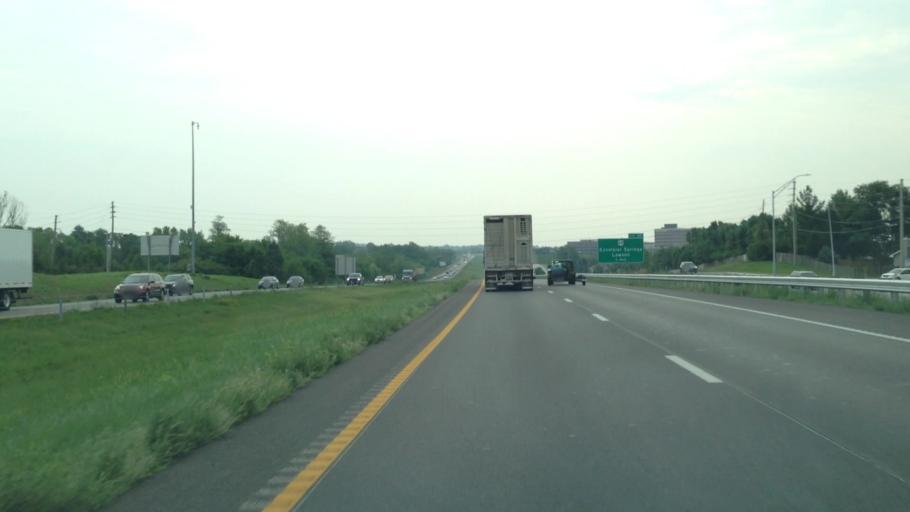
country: US
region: Missouri
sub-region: Clay County
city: Liberty
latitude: 39.2694
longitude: -94.4370
